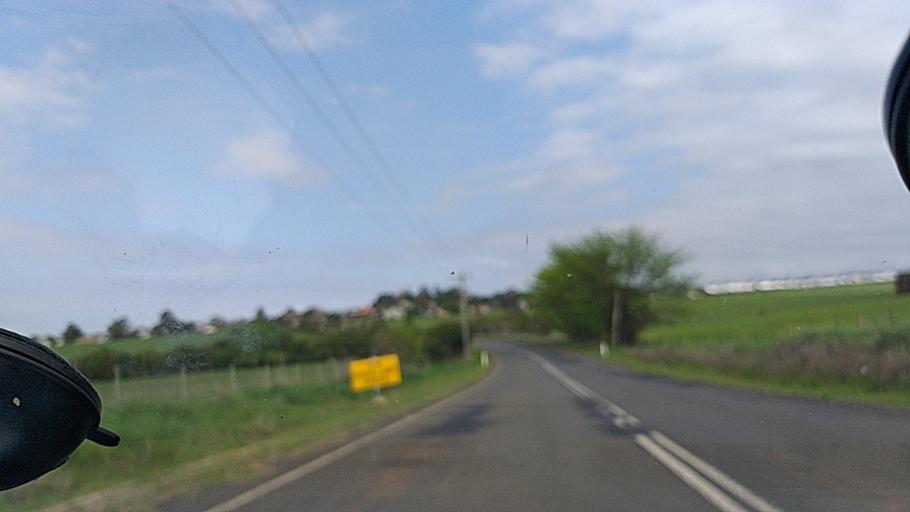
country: AU
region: New South Wales
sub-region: Camden
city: Camden South
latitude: -34.1251
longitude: 150.7313
